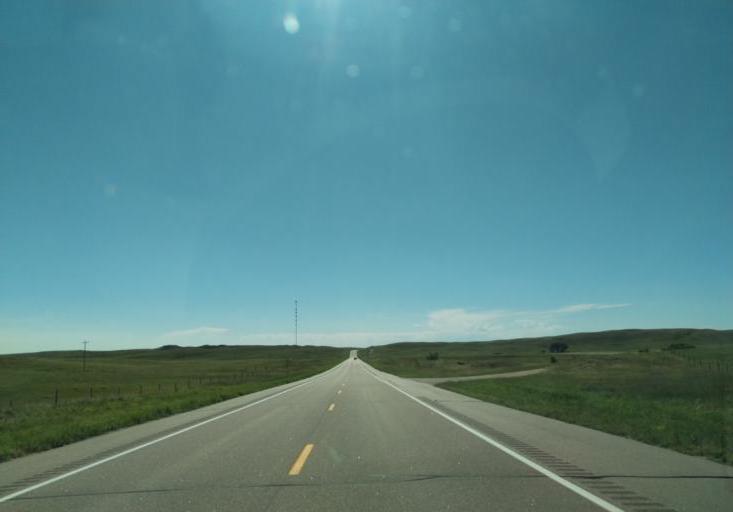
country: US
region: South Dakota
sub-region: Bennett County
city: Martin
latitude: 42.9210
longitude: -101.4534
